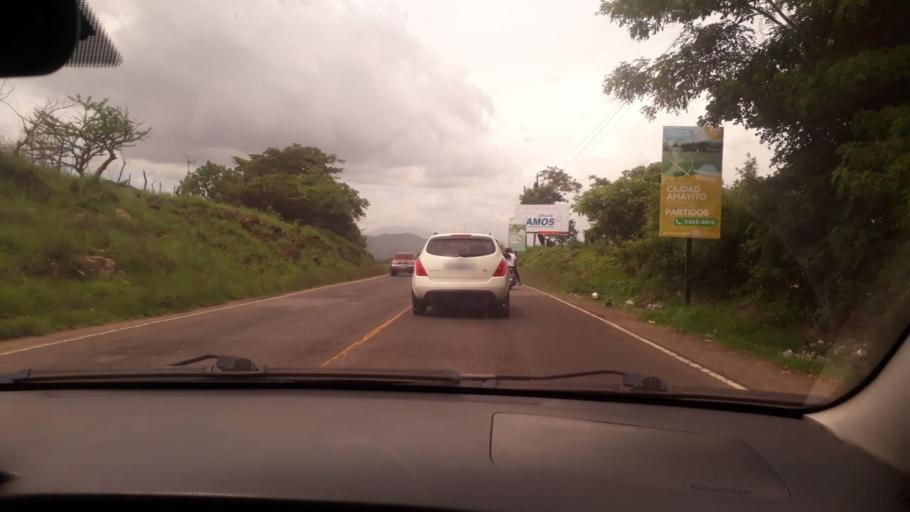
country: GT
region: Jutiapa
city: Quesada
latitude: 14.2758
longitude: -89.9694
